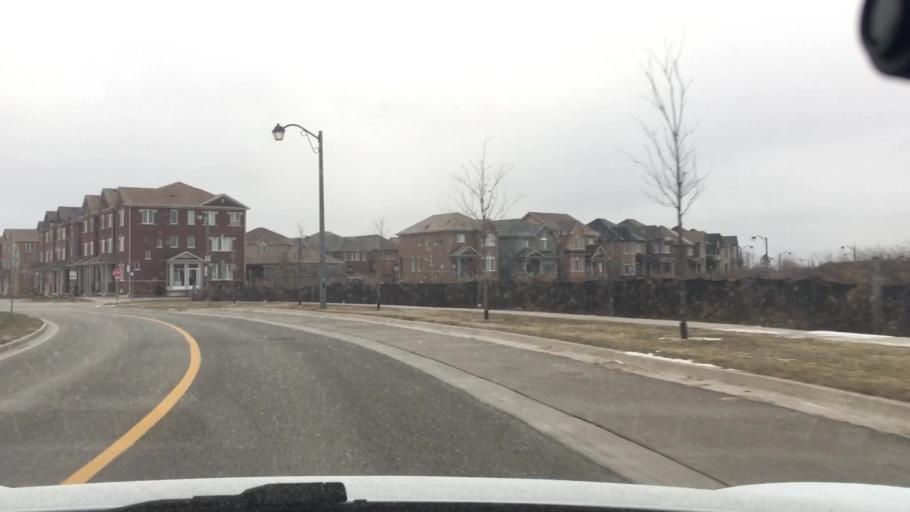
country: CA
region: Ontario
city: Markham
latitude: 43.8918
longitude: -79.2206
